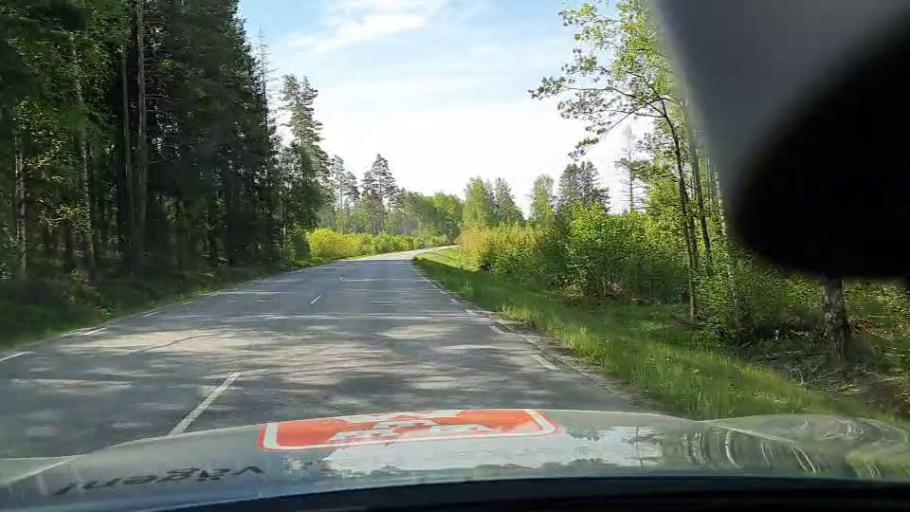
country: SE
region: Soedermanland
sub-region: Eskilstuna Kommun
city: Arla
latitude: 59.2965
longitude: 16.6768
